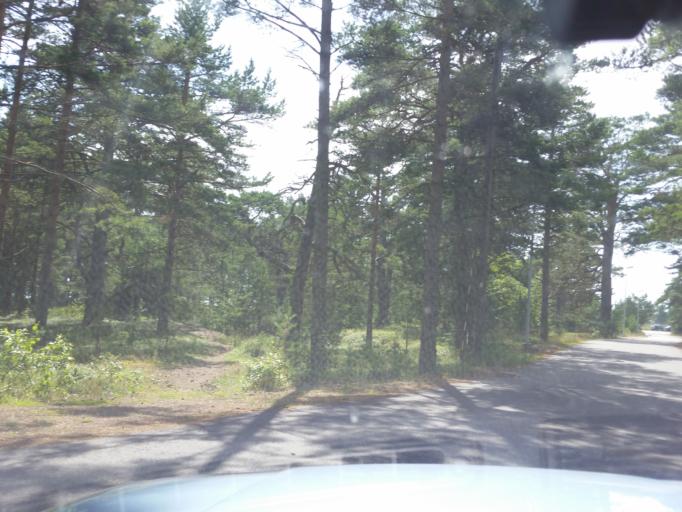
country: FI
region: Uusimaa
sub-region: Raaseporin
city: Hanko
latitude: 59.8263
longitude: 23.0086
